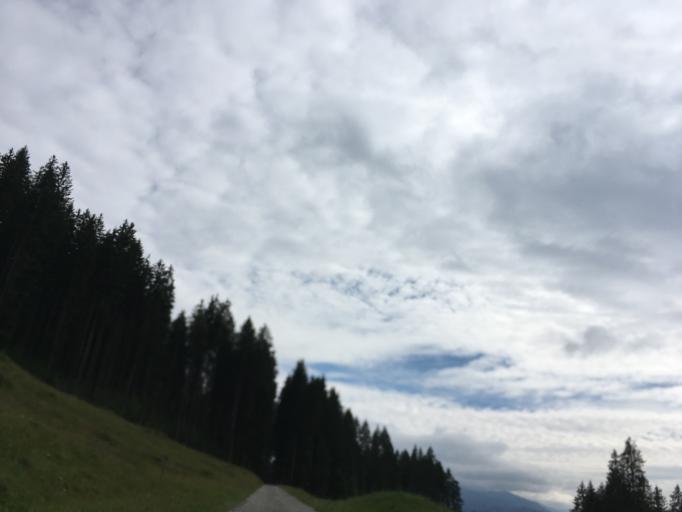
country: CH
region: Bern
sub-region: Interlaken-Oberhasli District
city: Beatenberg
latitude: 46.7097
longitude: 7.8136
